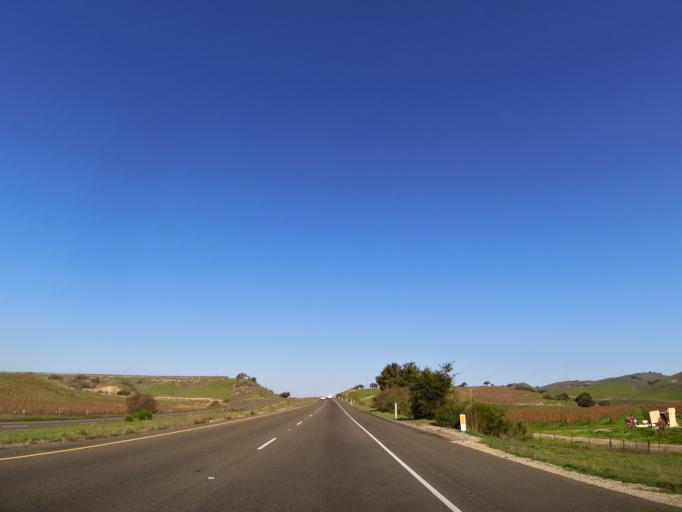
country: US
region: California
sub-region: Santa Barbara County
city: Los Alamos
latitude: 34.7645
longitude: -120.3020
